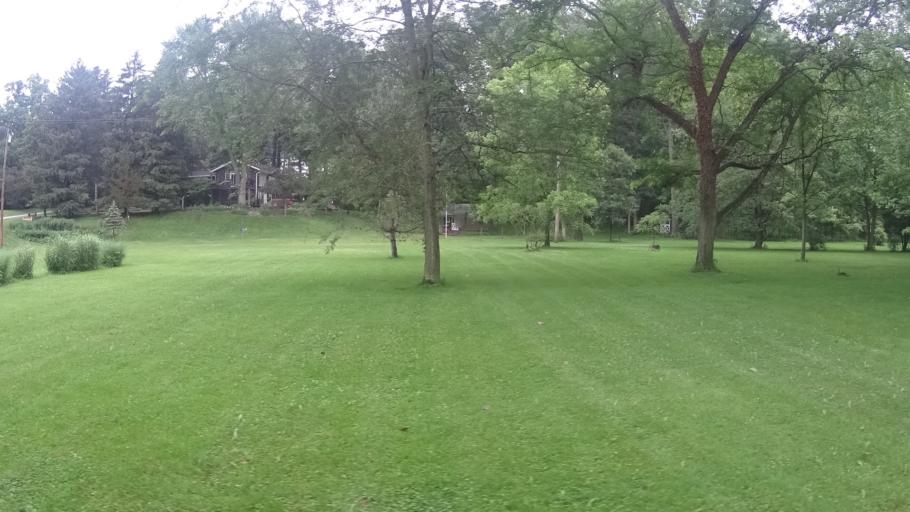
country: US
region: Ohio
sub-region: Erie County
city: Huron
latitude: 41.3578
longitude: -82.5851
